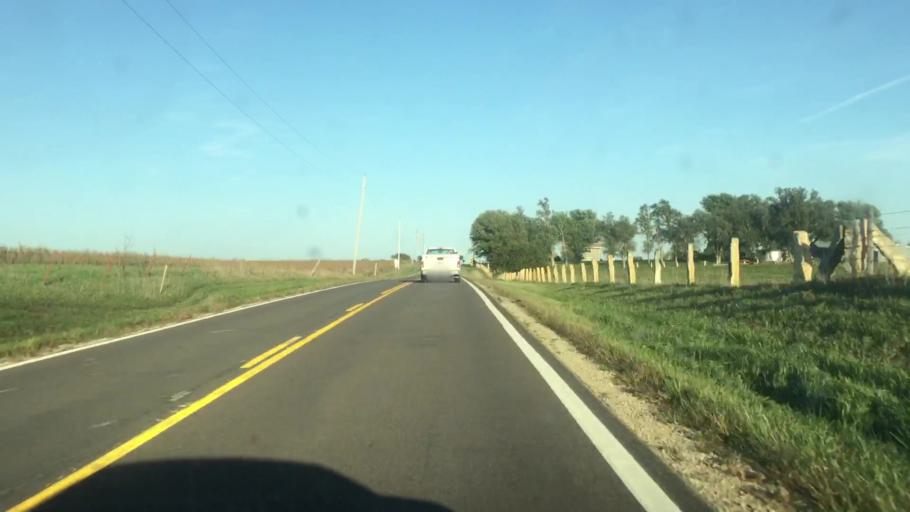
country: US
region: Kansas
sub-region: Brown County
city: Horton
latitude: 39.5517
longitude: -95.4524
